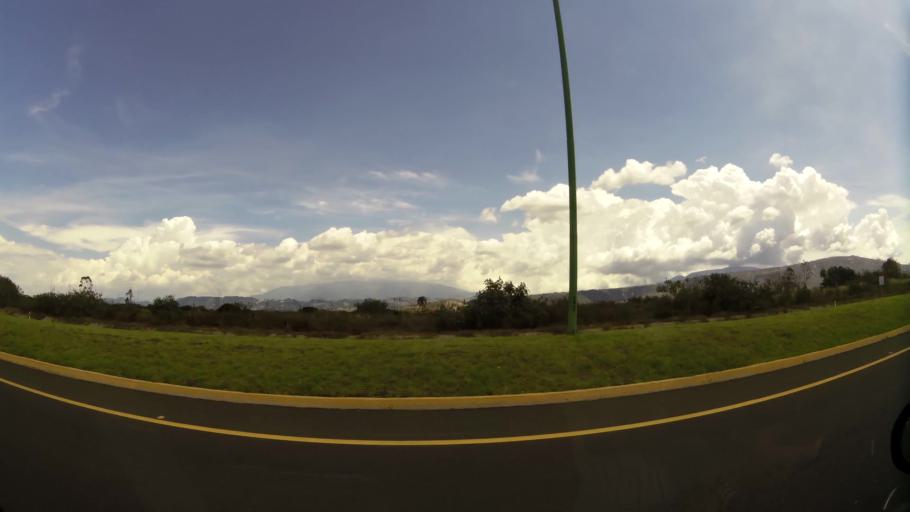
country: EC
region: Pichincha
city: Quito
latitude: -0.1199
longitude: -78.3652
